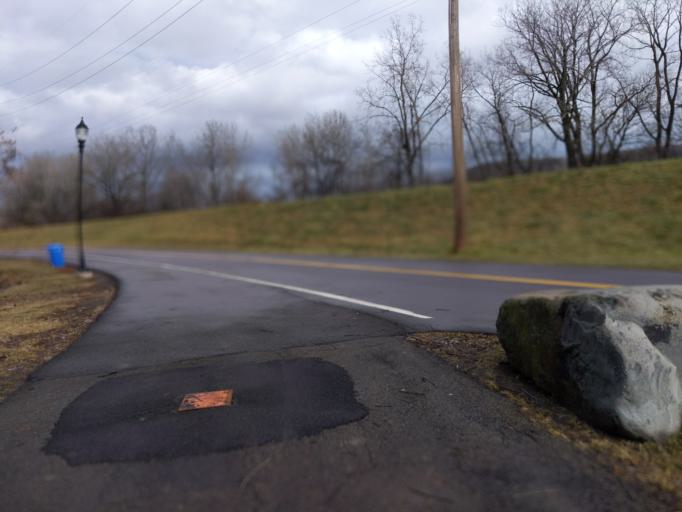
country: US
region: New York
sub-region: Chemung County
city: Elmira Heights
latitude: 42.1130
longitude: -76.8152
